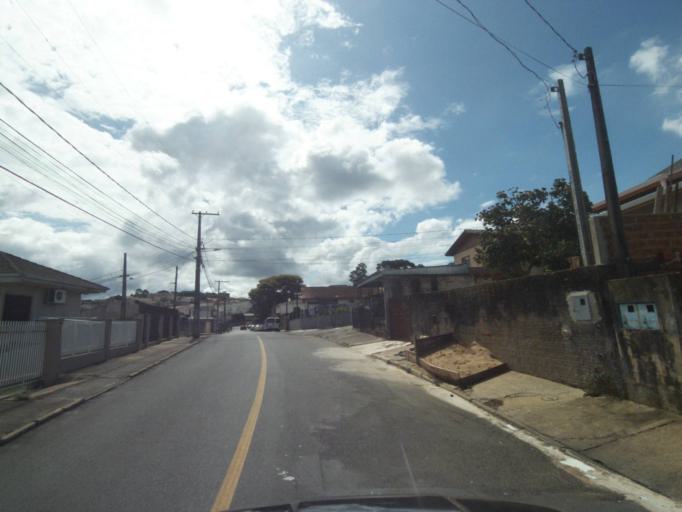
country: BR
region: Parana
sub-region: Telemaco Borba
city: Telemaco Borba
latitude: -24.3178
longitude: -50.6285
